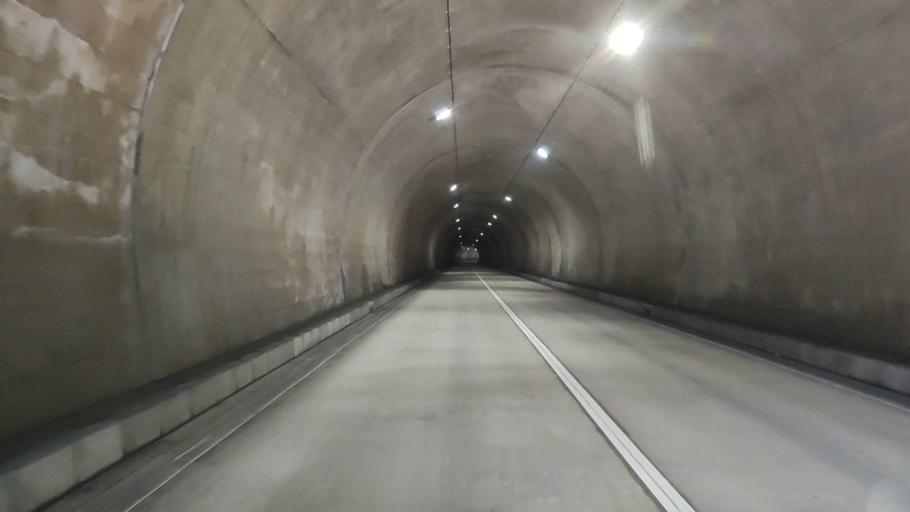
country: JP
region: Wakayama
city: Shingu
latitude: 33.8707
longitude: 135.8569
